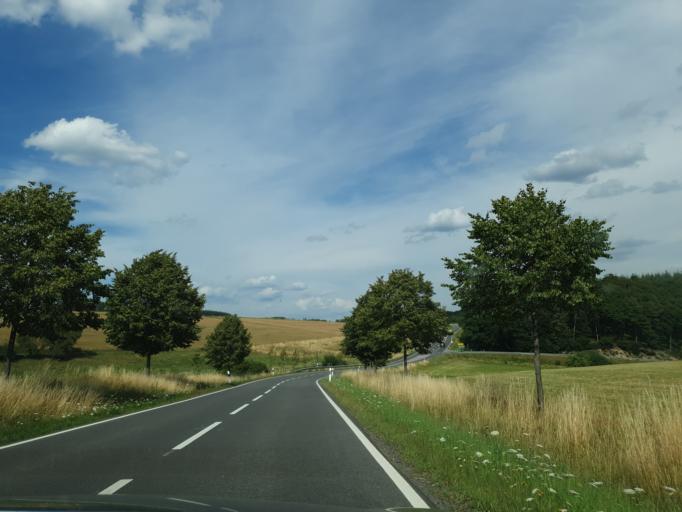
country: DE
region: Rheinland-Pfalz
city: Lind
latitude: 50.3159
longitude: 7.0261
